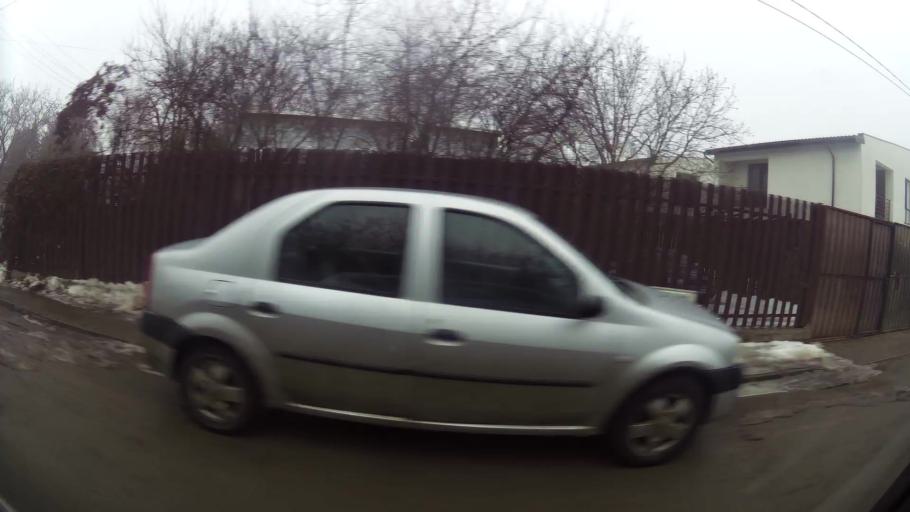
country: RO
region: Ilfov
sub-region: Comuna Chiajna
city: Chiajna
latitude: 44.4545
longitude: 25.9676
